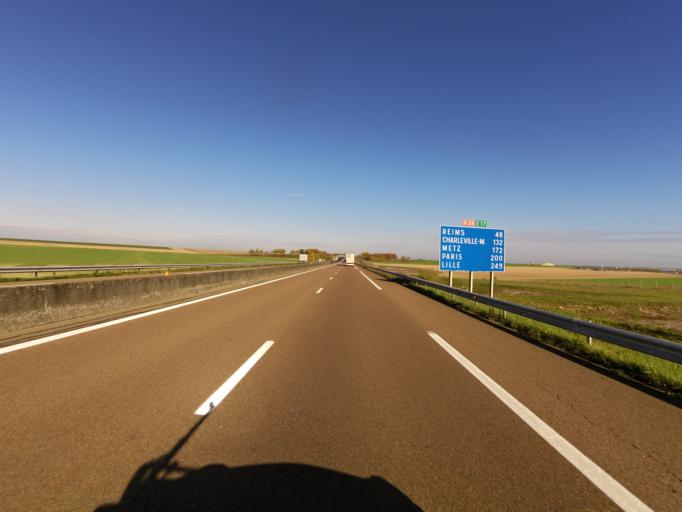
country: FR
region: Champagne-Ardenne
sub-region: Departement de la Marne
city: Fagnieres
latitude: 48.9175
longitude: 4.2834
